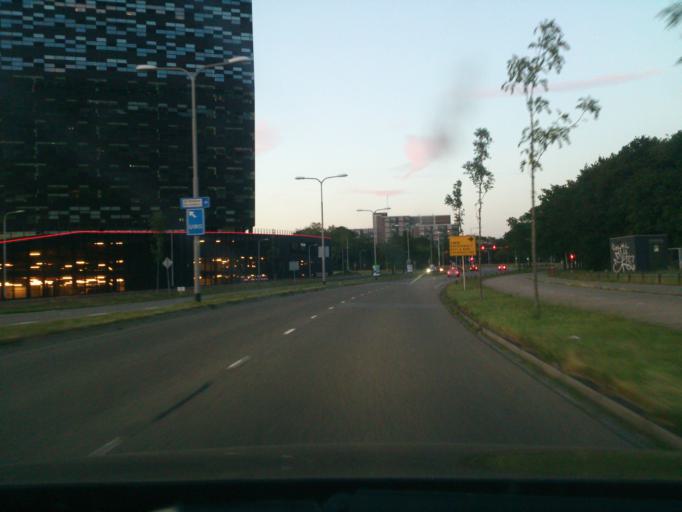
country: NL
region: Gelderland
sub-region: Gemeente Nijmegen
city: Lindenholt
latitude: 51.8235
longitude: 5.8242
